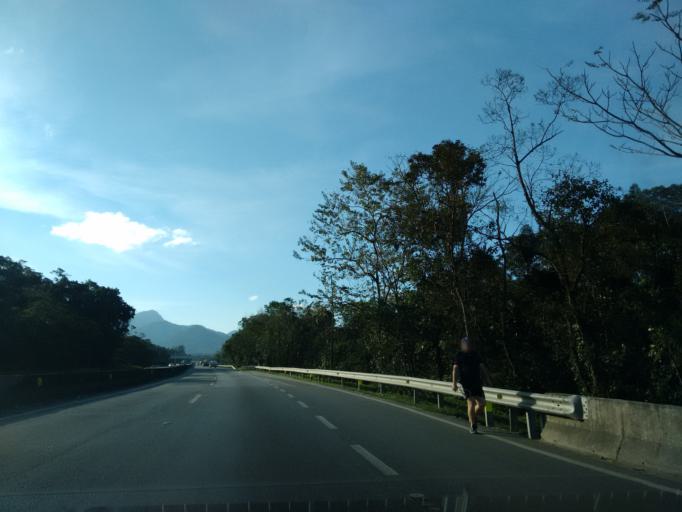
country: BR
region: Santa Catarina
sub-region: Joinville
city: Joinville
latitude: -26.0563
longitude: -48.8595
